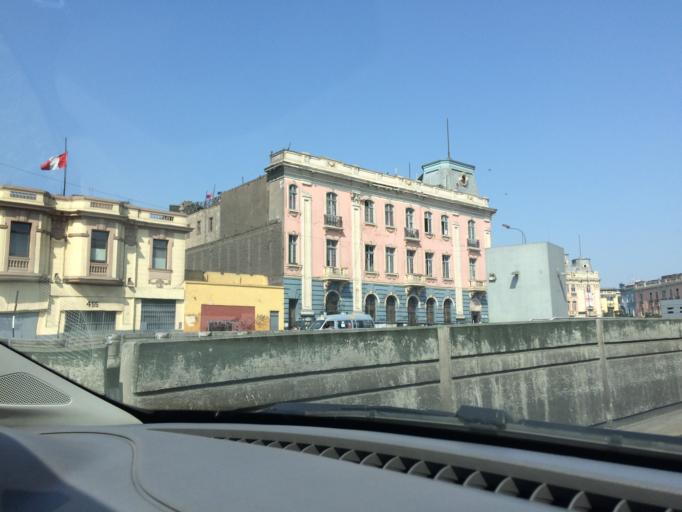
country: PE
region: Lima
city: Lima
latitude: -12.0453
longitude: -77.0430
